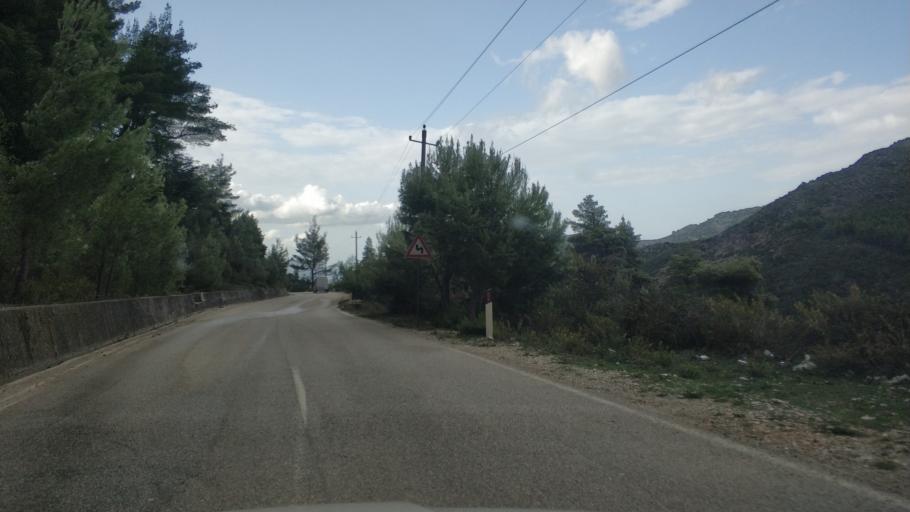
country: AL
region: Vlore
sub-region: Rrethi i Vlores
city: Orikum
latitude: 40.2585
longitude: 19.5269
